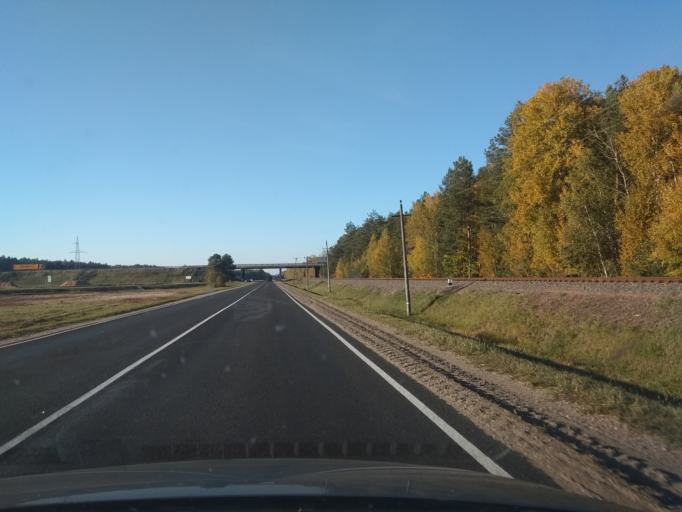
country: BY
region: Brest
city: Nyakhachava
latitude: 52.5737
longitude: 25.1142
